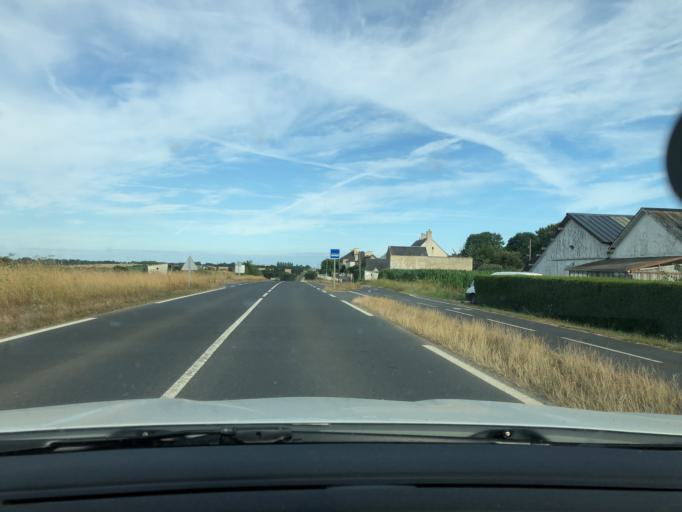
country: FR
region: Lower Normandy
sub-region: Departement du Calvados
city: Saint-Vigor-le-Grand
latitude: 49.2490
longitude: -0.6243
